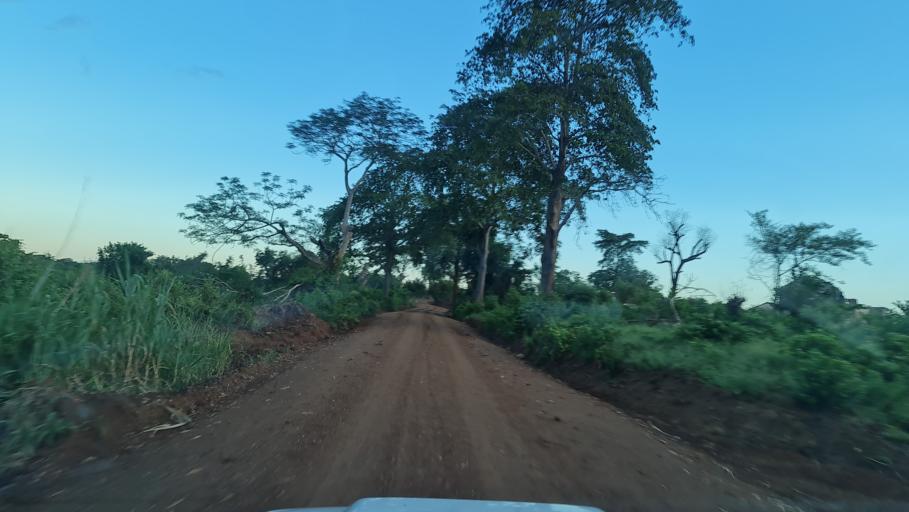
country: MZ
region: Nampula
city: Ilha de Mocambique
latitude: -14.9804
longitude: 40.0937
